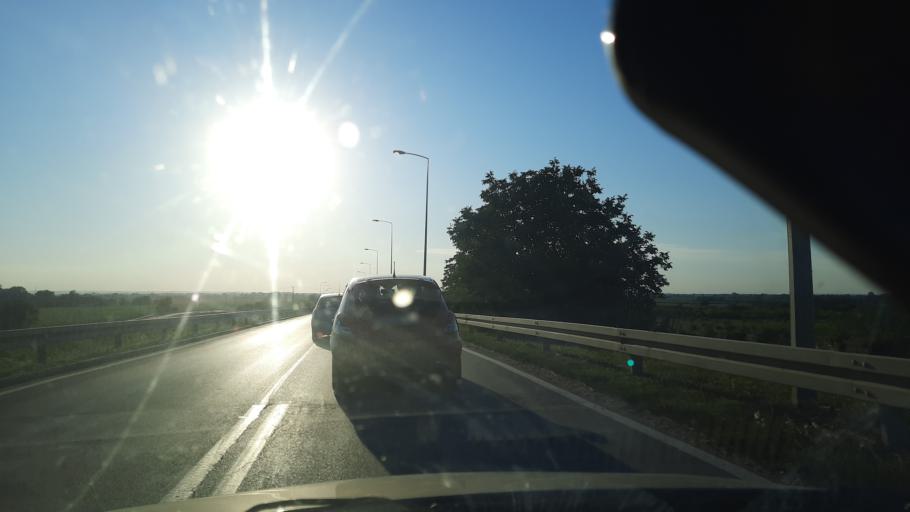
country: RS
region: Central Serbia
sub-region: Branicevski Okrug
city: Pozarevac
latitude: 44.5981
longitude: 21.1528
